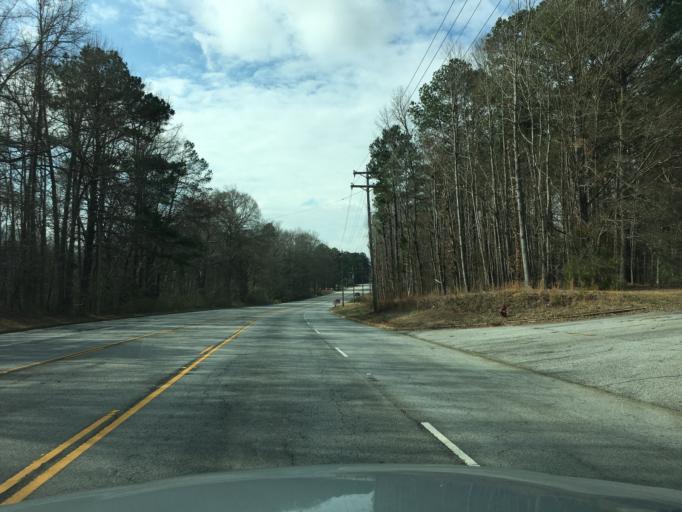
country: US
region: South Carolina
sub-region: Laurens County
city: Clinton
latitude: 34.4565
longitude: -81.8691
